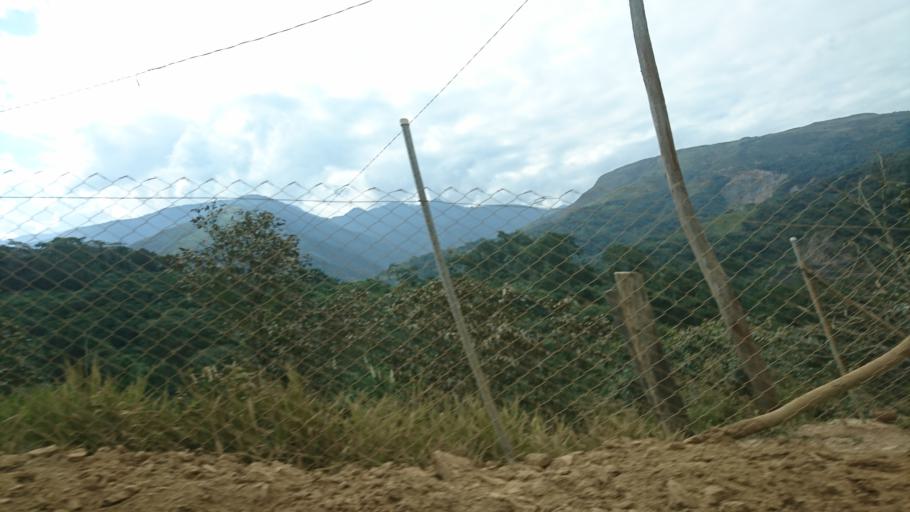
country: BO
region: La Paz
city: Coroico
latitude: -16.1645
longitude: -67.7288
